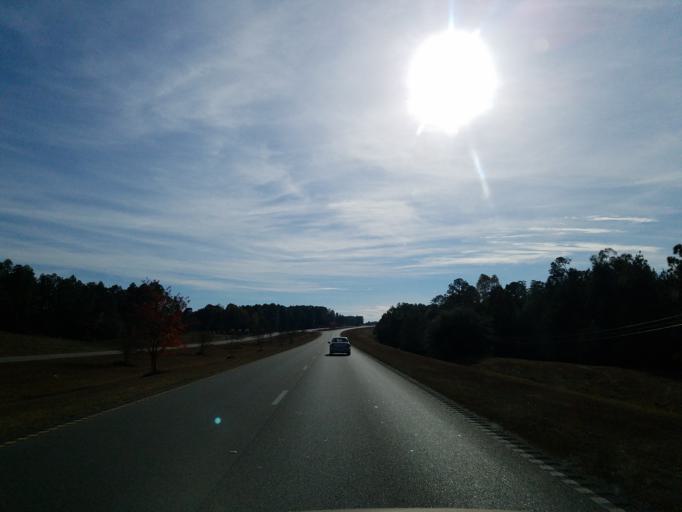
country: US
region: Mississippi
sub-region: Lamar County
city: West Hattiesburg
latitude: 31.2749
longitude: -89.3290
